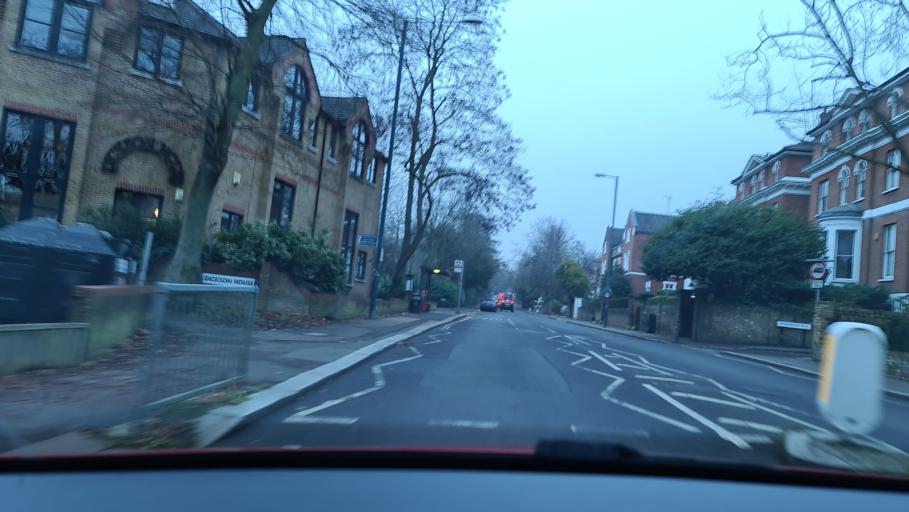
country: GB
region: England
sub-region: Greater London
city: Richmond
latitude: 51.4544
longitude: -0.2935
